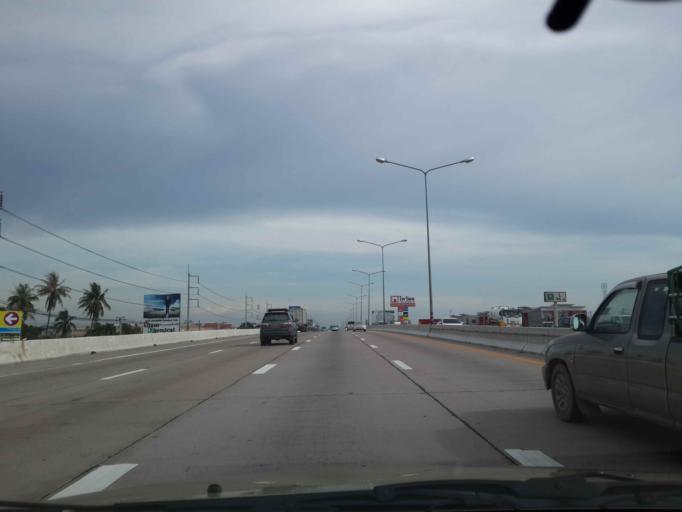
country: TH
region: Chon Buri
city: Si Racha
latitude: 13.1466
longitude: 100.9859
